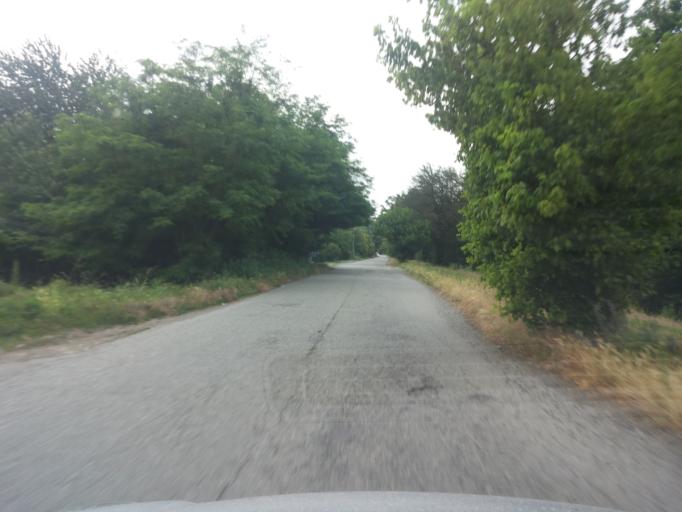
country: IT
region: Piedmont
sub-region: Provincia di Biella
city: Cavaglia
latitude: 45.3854
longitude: 8.1281
